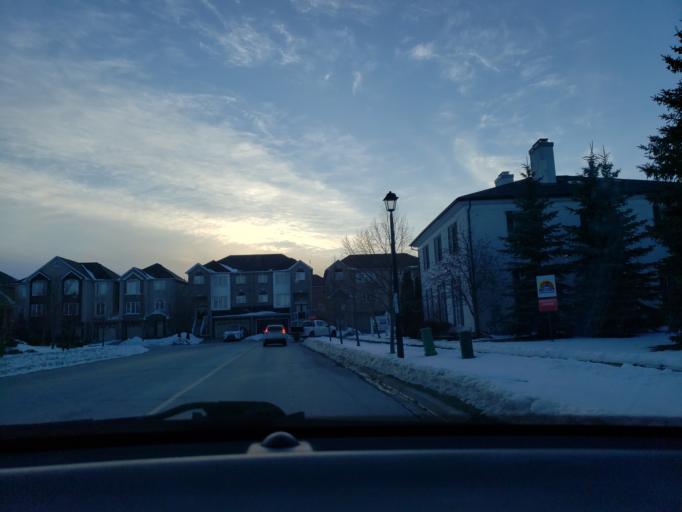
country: CA
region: Ontario
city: Newmarket
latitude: 44.0604
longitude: -79.4854
